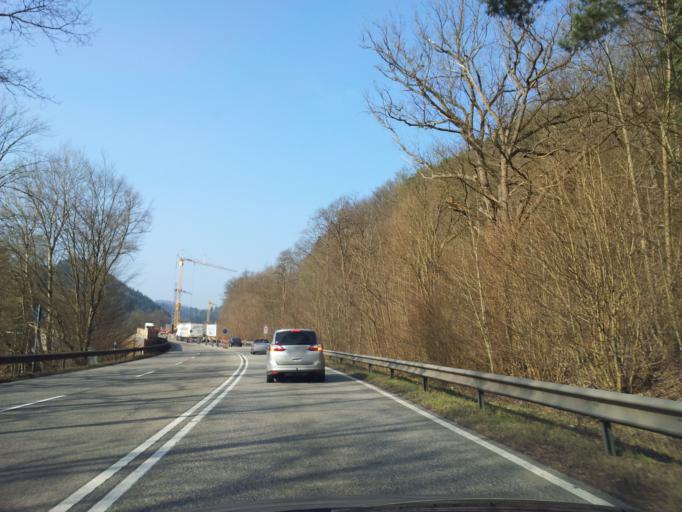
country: DE
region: Rheinland-Pfalz
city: Hinterweidenthal
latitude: 49.2016
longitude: 7.7593
